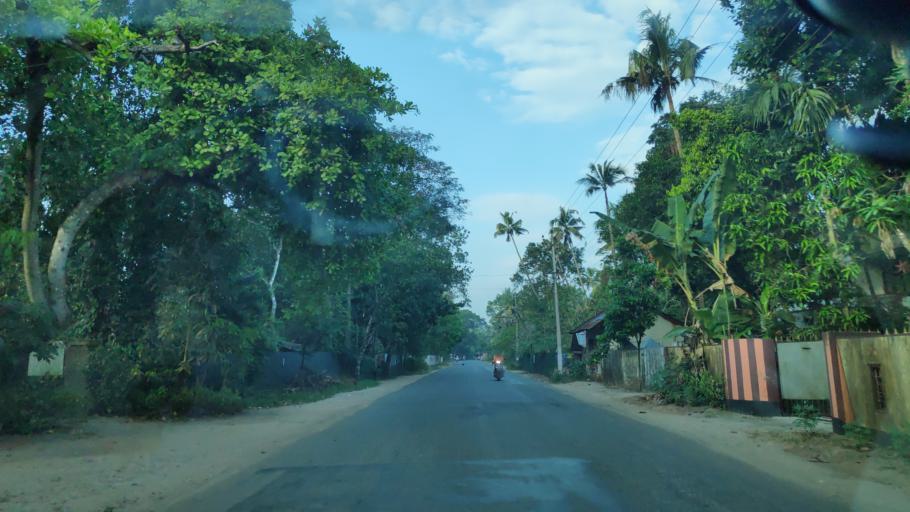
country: IN
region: Kerala
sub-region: Alappuzha
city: Shertallai
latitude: 9.6201
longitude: 76.3642
